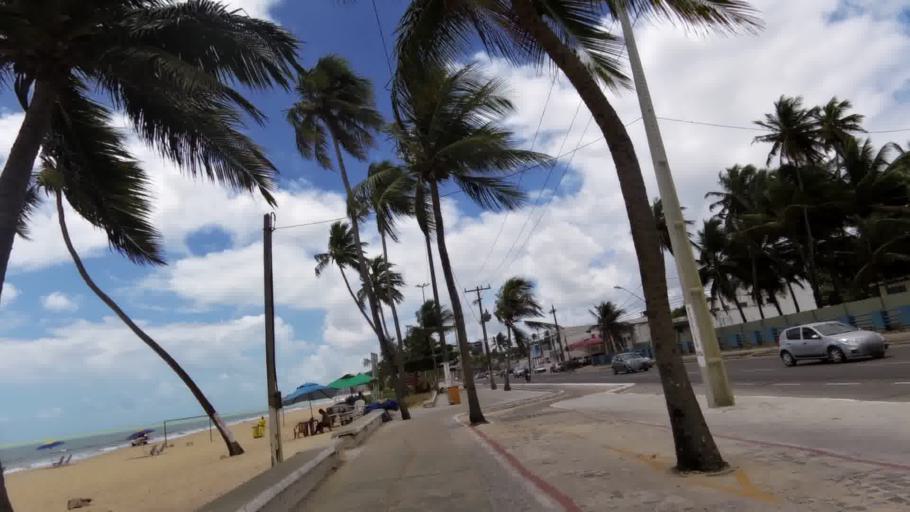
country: BR
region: Pernambuco
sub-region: Jaboatao Dos Guararapes
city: Jaboatao
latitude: -8.1584
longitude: -34.9107
